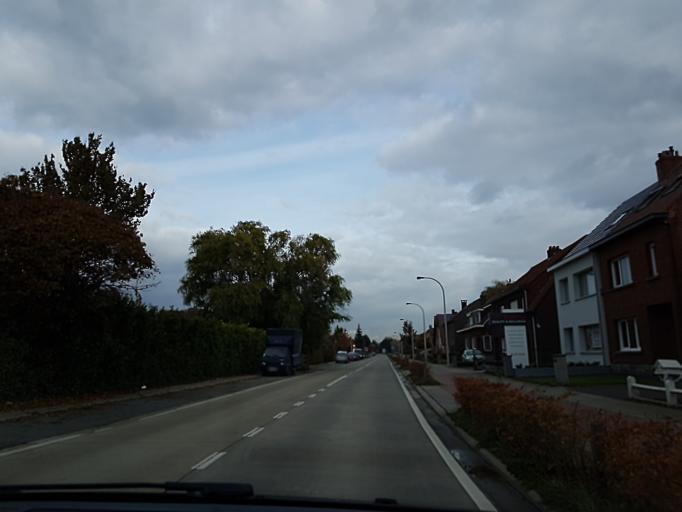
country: BE
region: Flanders
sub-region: Provincie Antwerpen
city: Ranst
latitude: 51.1840
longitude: 4.5613
